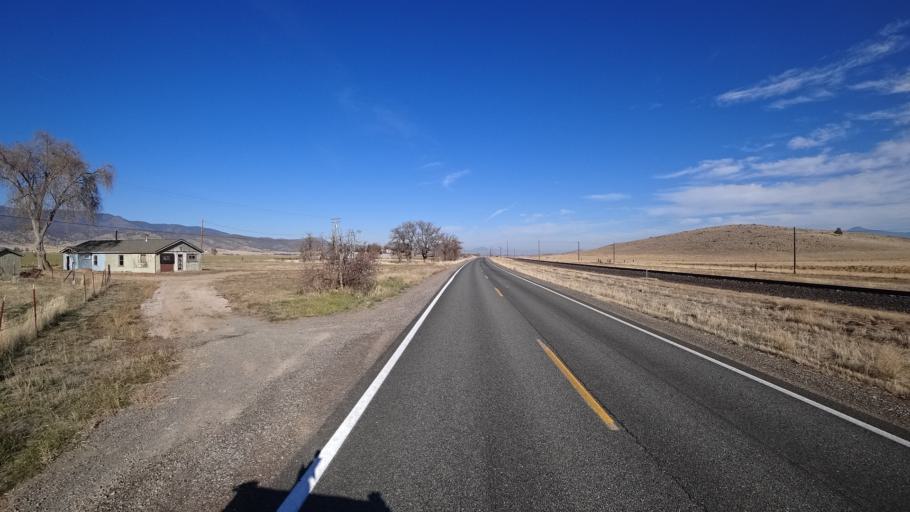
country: US
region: California
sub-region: Siskiyou County
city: Montague
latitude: 41.5516
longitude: -122.5262
